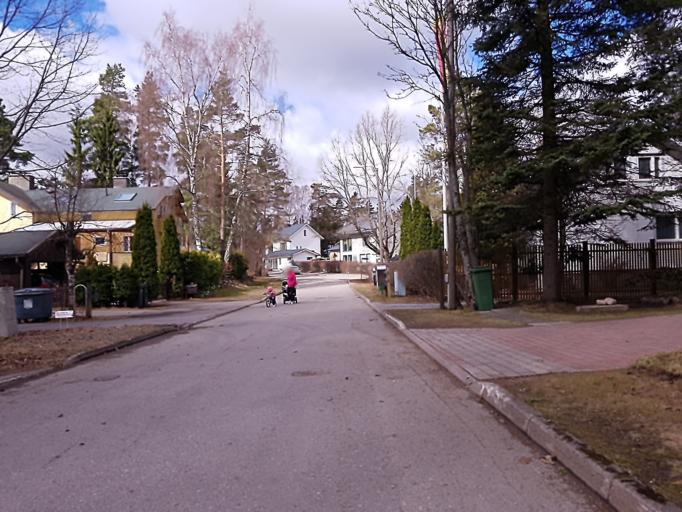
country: FI
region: Uusimaa
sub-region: Helsinki
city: Helsinki
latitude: 60.2451
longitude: 24.9025
